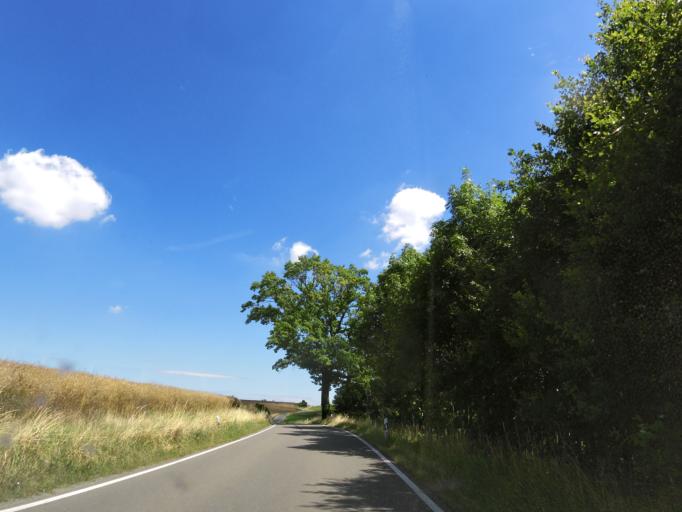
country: DE
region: Thuringia
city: Kraftsdorf
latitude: 50.8841
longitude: 11.9347
